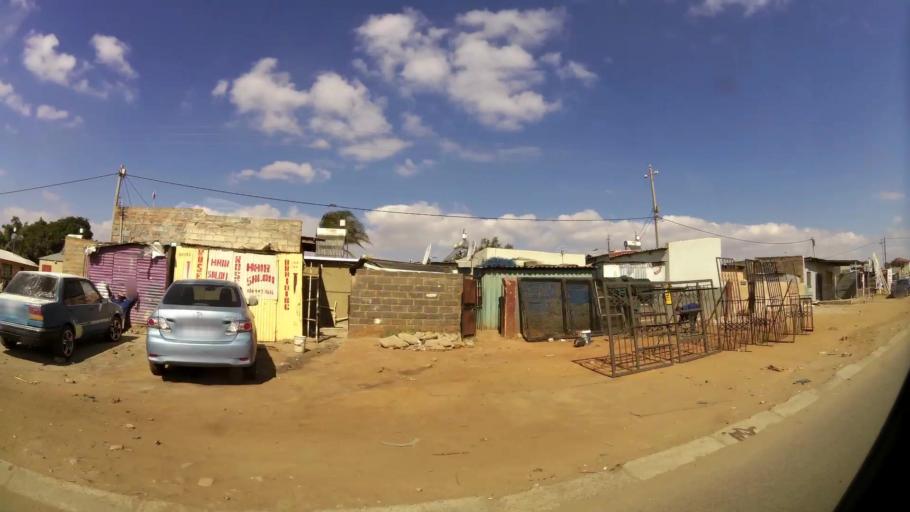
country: ZA
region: Gauteng
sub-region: City of Johannesburg Metropolitan Municipality
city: Midrand
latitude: -26.0131
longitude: 28.1760
